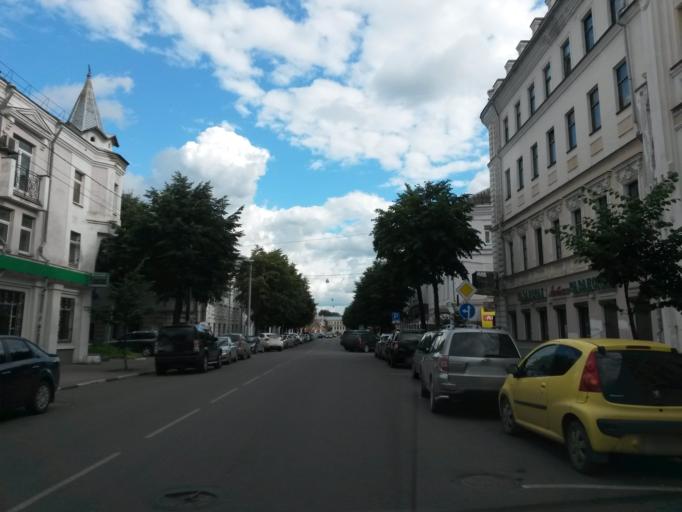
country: RU
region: Jaroslavl
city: Yaroslavl
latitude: 57.6272
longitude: 39.8883
